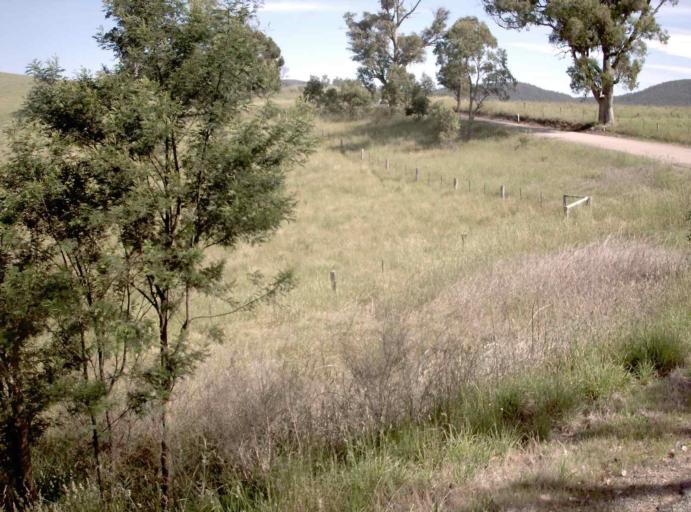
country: AU
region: Victoria
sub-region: East Gippsland
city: Lakes Entrance
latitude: -37.4960
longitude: 148.1333
